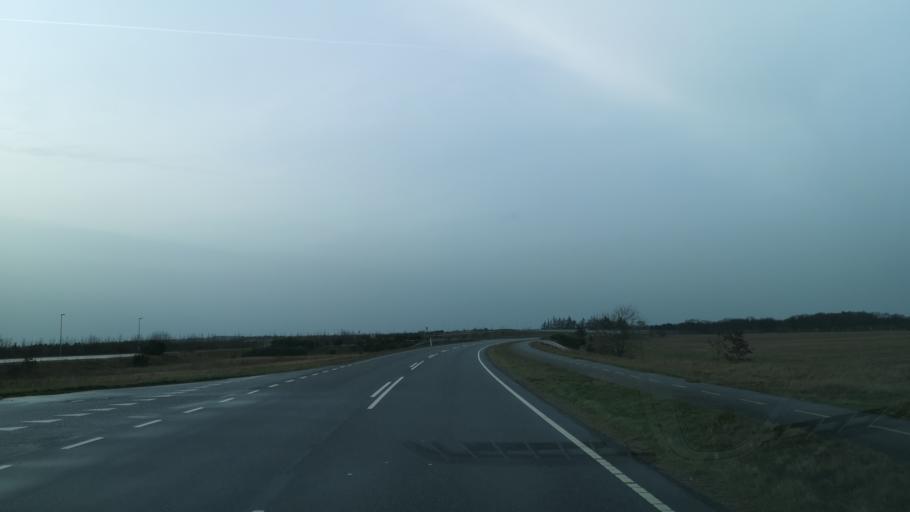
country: DK
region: Central Jutland
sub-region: Herning Kommune
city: Lind
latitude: 56.0124
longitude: 9.0333
